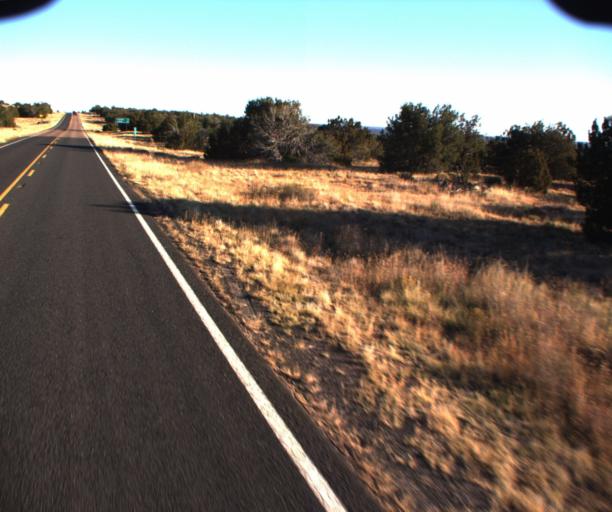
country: US
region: Arizona
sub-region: Apache County
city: Ganado
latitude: 35.4420
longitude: -109.5224
